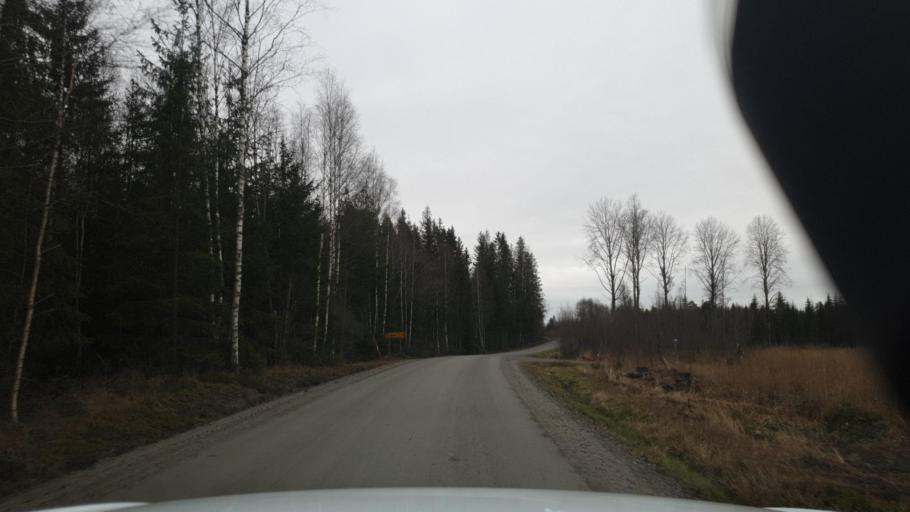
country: SE
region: Vaermland
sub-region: Karlstads Kommun
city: Edsvalla
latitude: 59.4819
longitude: 13.0738
